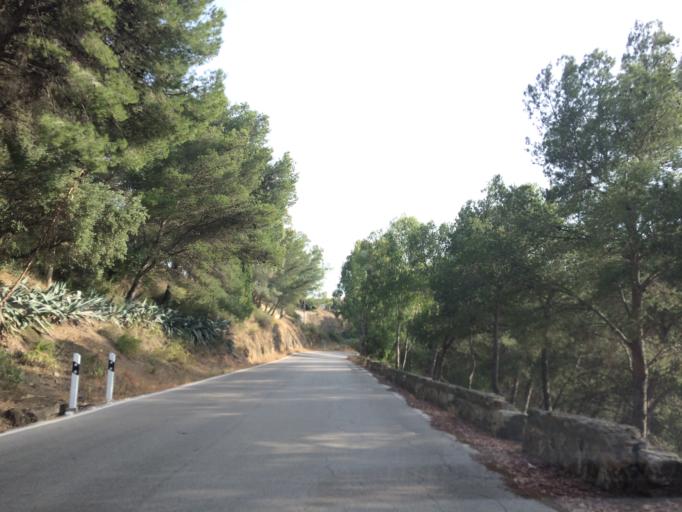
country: ES
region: Andalusia
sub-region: Provincia de Malaga
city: Malaga
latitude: 36.7708
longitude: -4.3881
